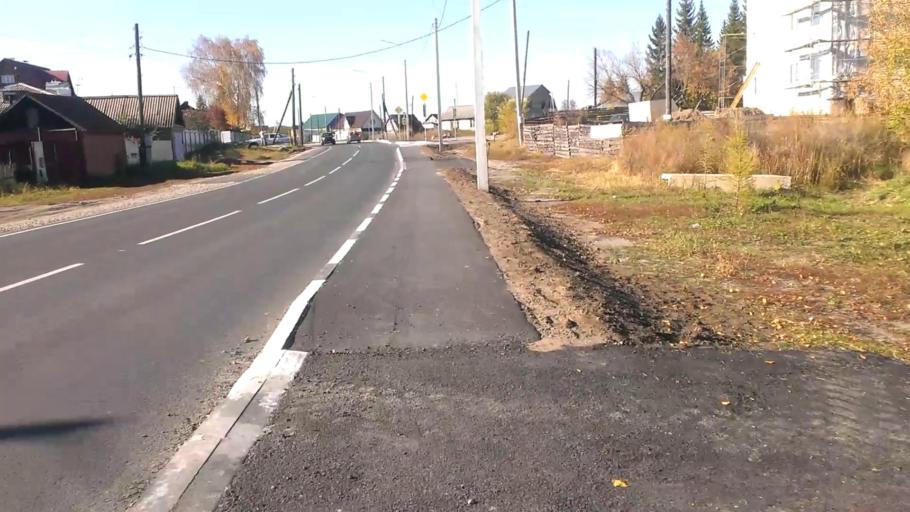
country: RU
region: Altai Krai
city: Sannikovo
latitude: 53.3155
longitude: 83.9594
